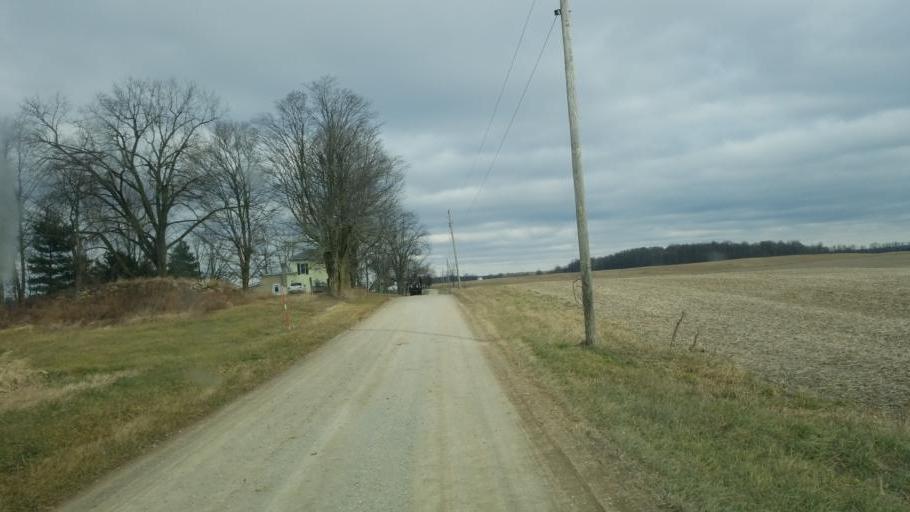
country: US
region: Ohio
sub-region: Richland County
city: Lexington
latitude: 40.5814
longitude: -82.6761
